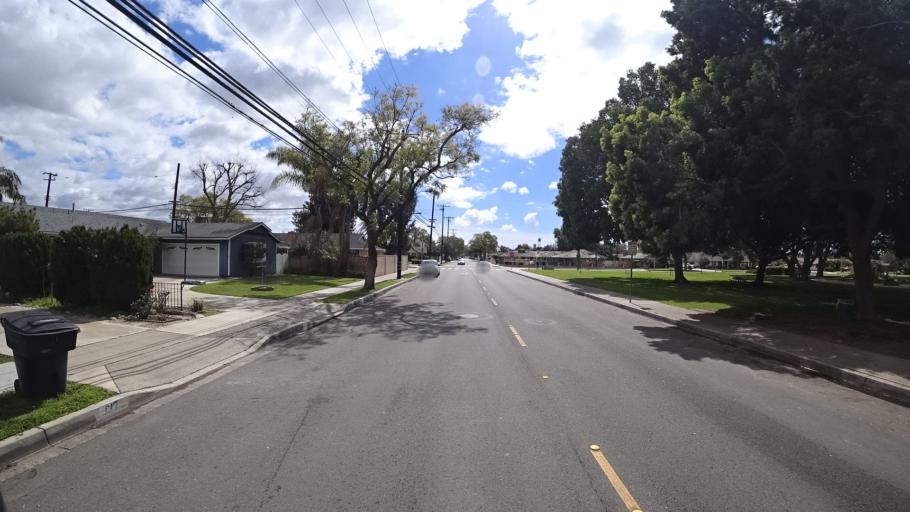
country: US
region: California
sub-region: Orange County
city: Anaheim
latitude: 33.8224
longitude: -117.9371
